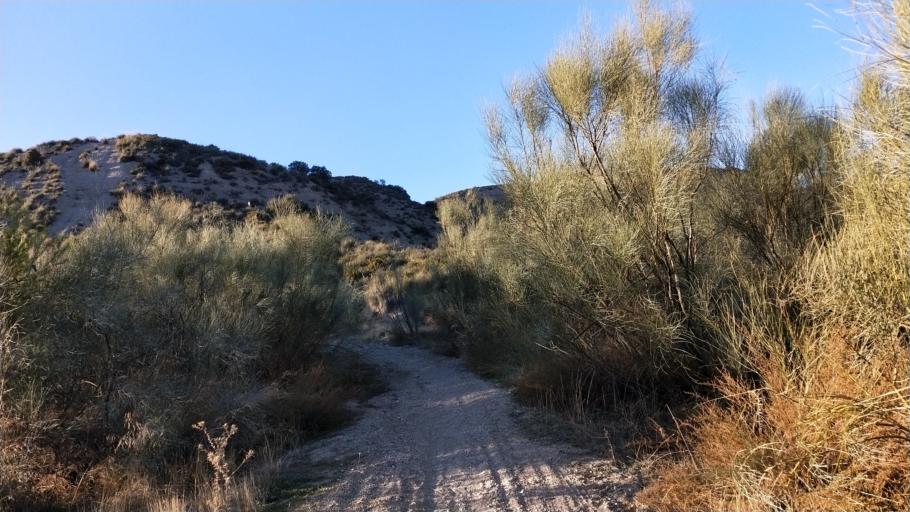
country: ES
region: Andalusia
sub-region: Provincia de Granada
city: Dudar
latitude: 37.1937
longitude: -3.4983
